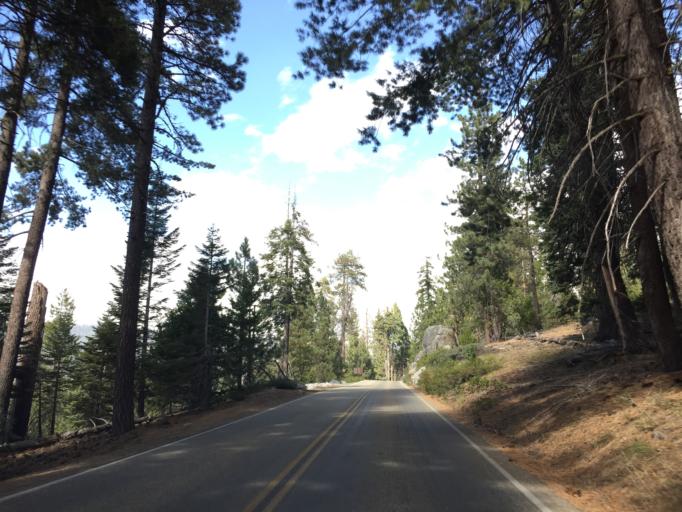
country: US
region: California
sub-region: Tulare County
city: Three Rivers
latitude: 36.5889
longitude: -118.7523
